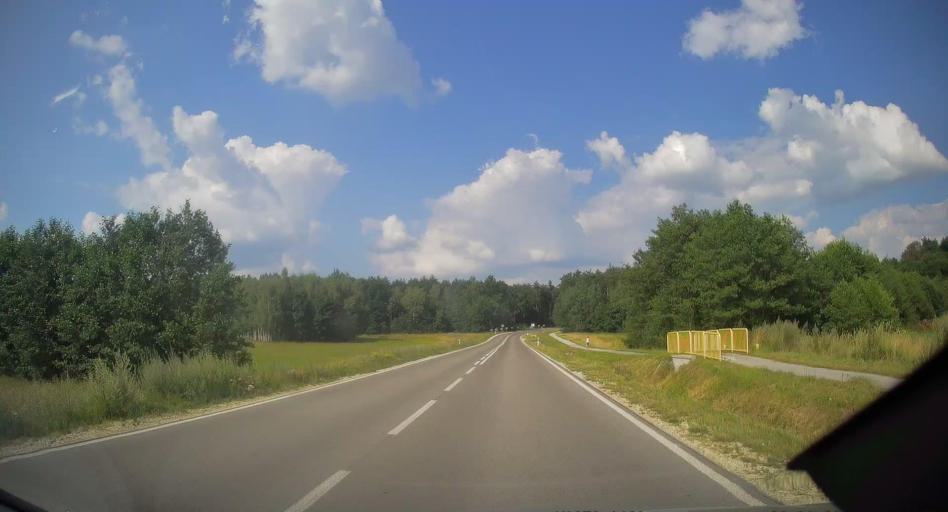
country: PL
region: Swietokrzyskie
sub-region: Powiat kielecki
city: Lopuszno
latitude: 51.0038
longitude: 20.2728
